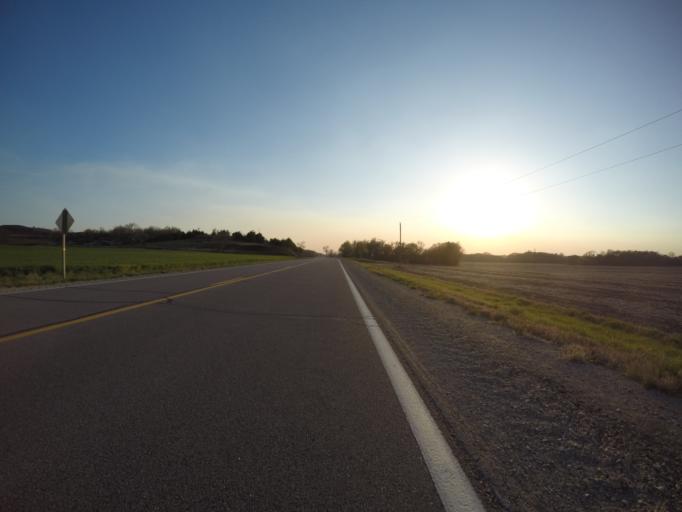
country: US
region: Kansas
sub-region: Riley County
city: Manhattan
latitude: 39.1104
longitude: -96.6174
